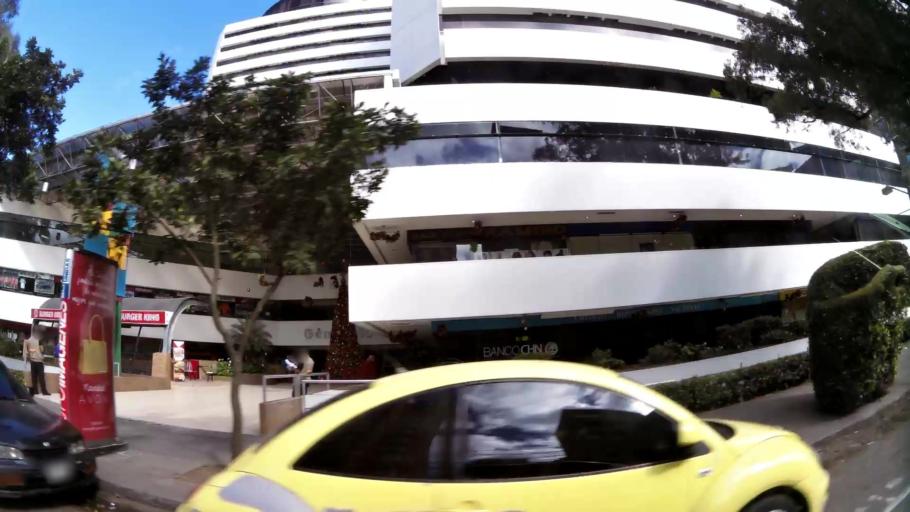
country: GT
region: Guatemala
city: Santa Catarina Pinula
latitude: 14.6008
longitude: -90.5149
